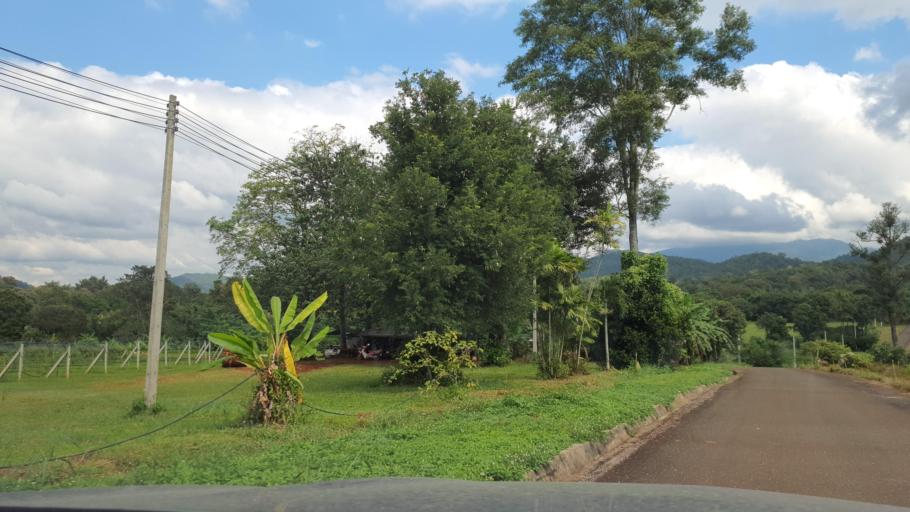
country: TH
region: Chiang Mai
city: Mae On
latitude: 18.8644
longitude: 99.2693
